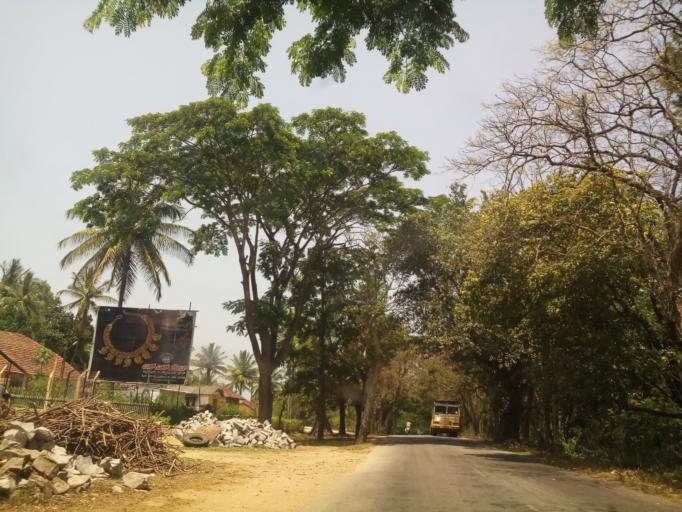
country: IN
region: Karnataka
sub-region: Hassan
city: Sakleshpur
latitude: 12.9546
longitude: 75.8518
